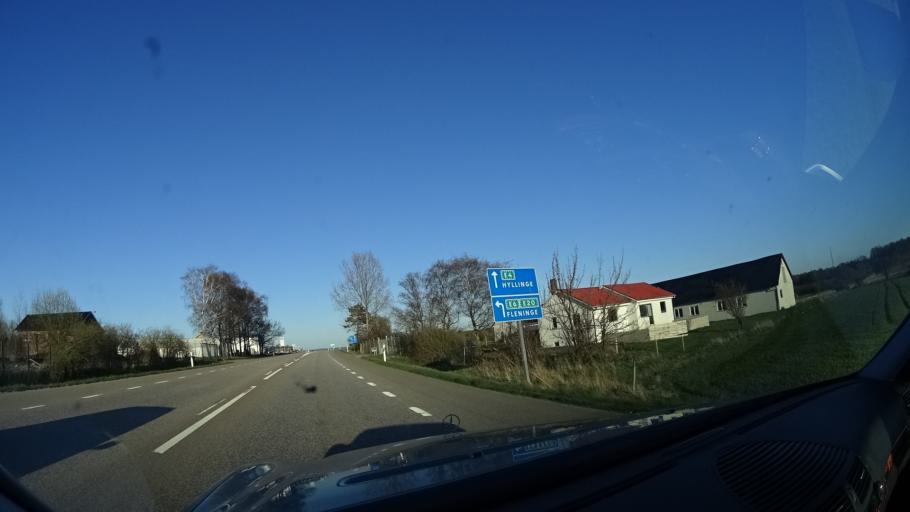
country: SE
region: Skane
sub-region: Helsingborg
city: Hyllinge
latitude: 56.0995
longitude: 12.8089
